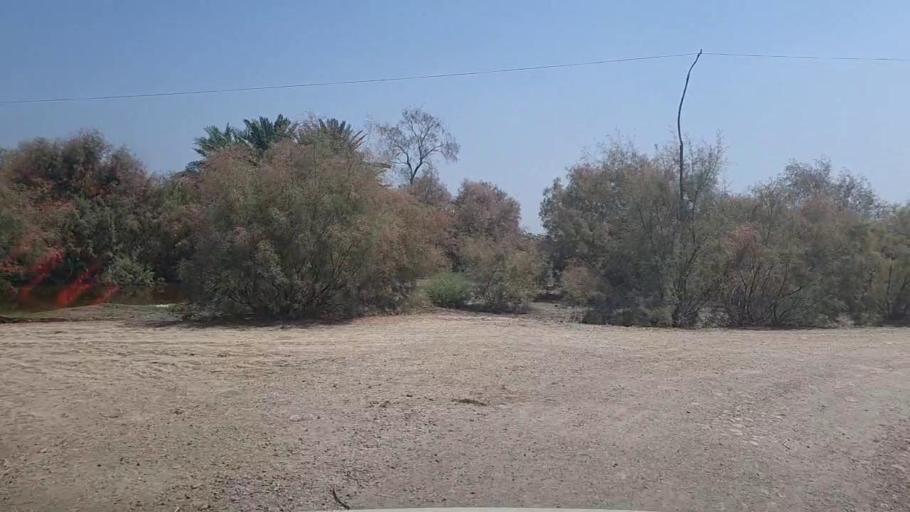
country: PK
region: Sindh
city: Kandhkot
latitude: 28.3062
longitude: 69.3584
